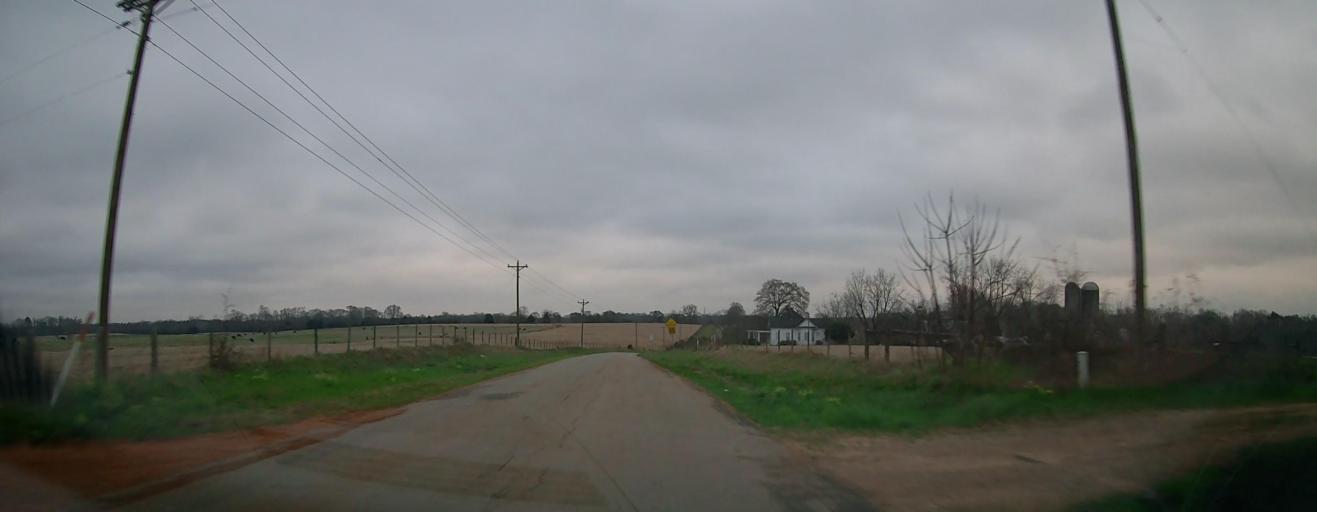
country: US
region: Georgia
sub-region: Monroe County
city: Forsyth
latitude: 32.9885
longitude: -84.0211
